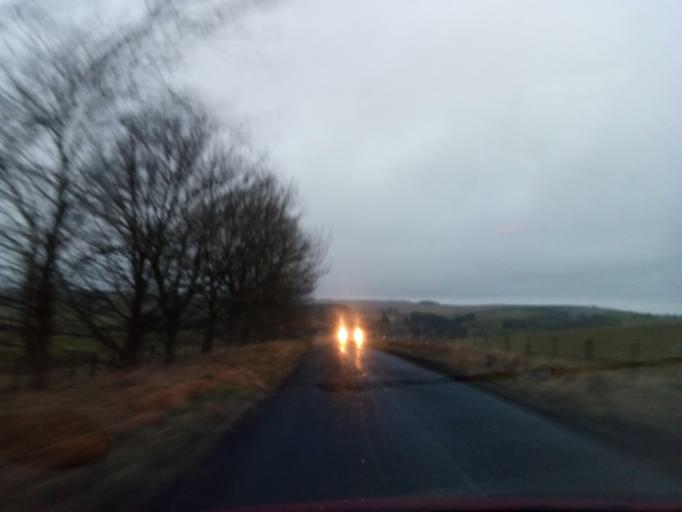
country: GB
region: England
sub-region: Northumberland
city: Otterburn
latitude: 55.2251
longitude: -2.0973
